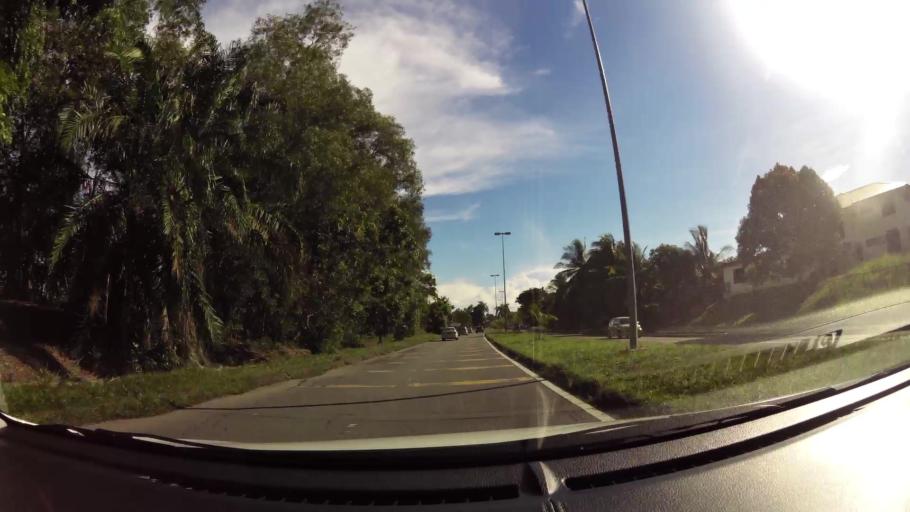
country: BN
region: Brunei and Muara
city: Bandar Seri Begawan
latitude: 4.9667
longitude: 114.9628
